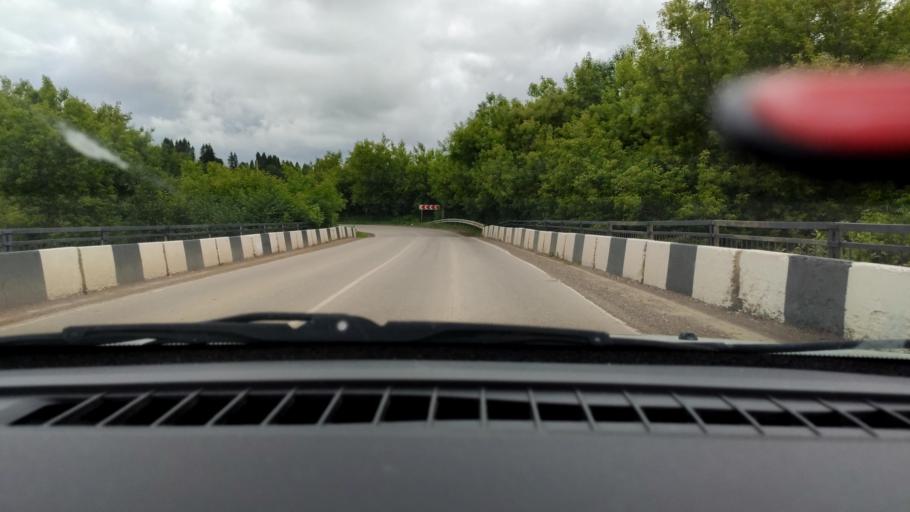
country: RU
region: Perm
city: Chaykovskaya
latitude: 58.1109
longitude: 55.5862
